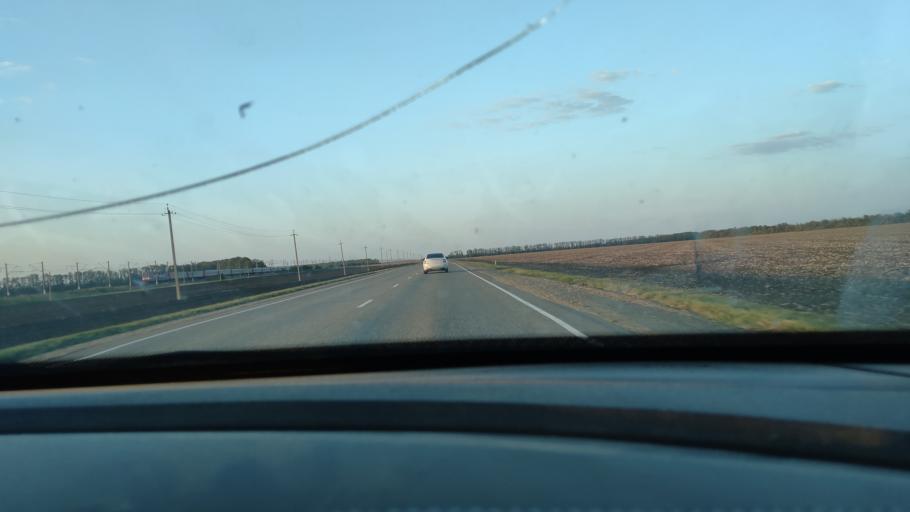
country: RU
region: Krasnodarskiy
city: Novominskaya
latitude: 46.3650
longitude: 38.9713
